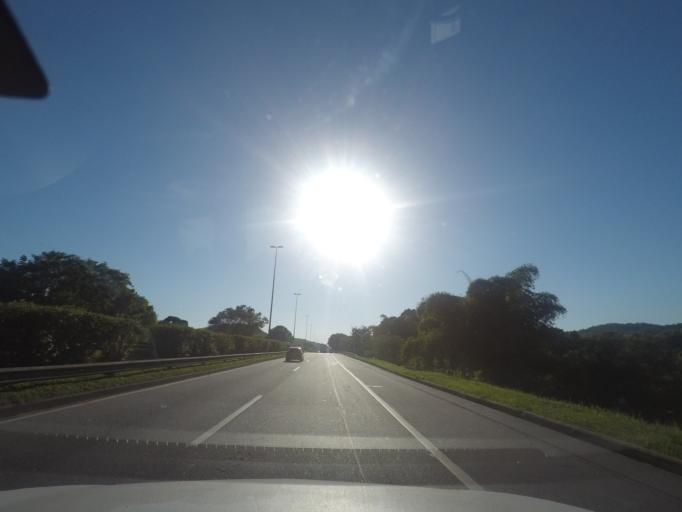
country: BR
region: Rio de Janeiro
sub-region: Petropolis
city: Petropolis
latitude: -22.6491
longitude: -43.1762
